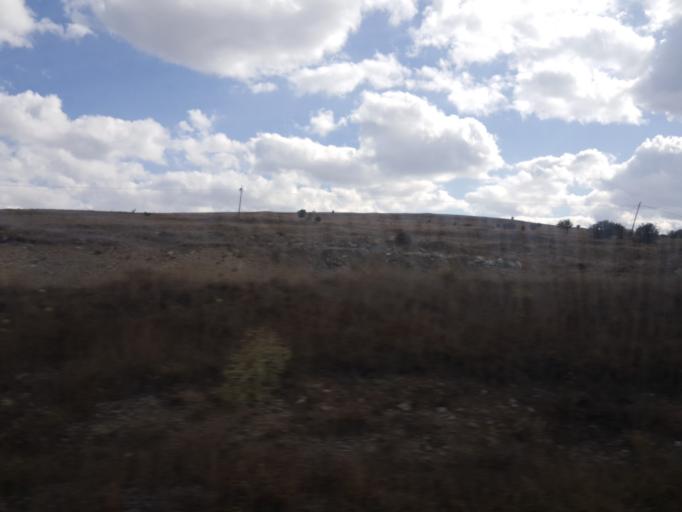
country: TR
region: Tokat
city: Yesilyurt
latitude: 40.0167
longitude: 36.2480
